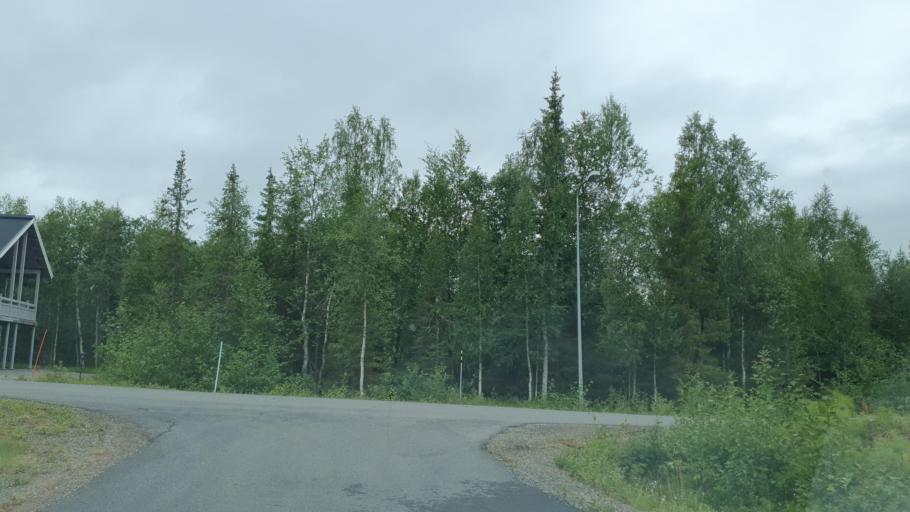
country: FI
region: Lapland
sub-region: Tunturi-Lappi
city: Kolari
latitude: 67.5935
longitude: 24.1732
